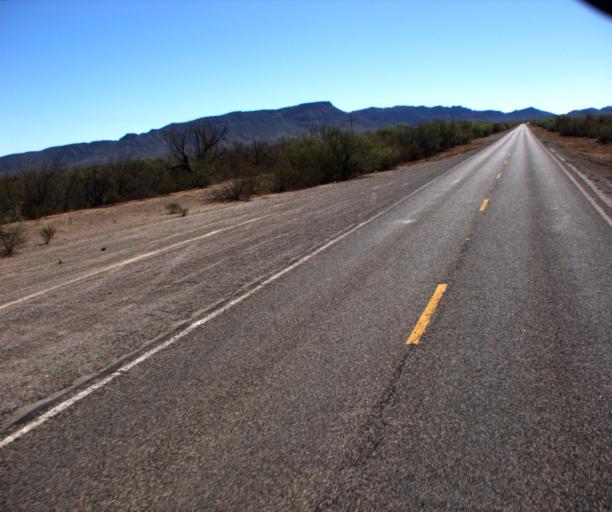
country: US
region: Arizona
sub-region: Pima County
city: Ajo
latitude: 32.3301
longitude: -112.7832
